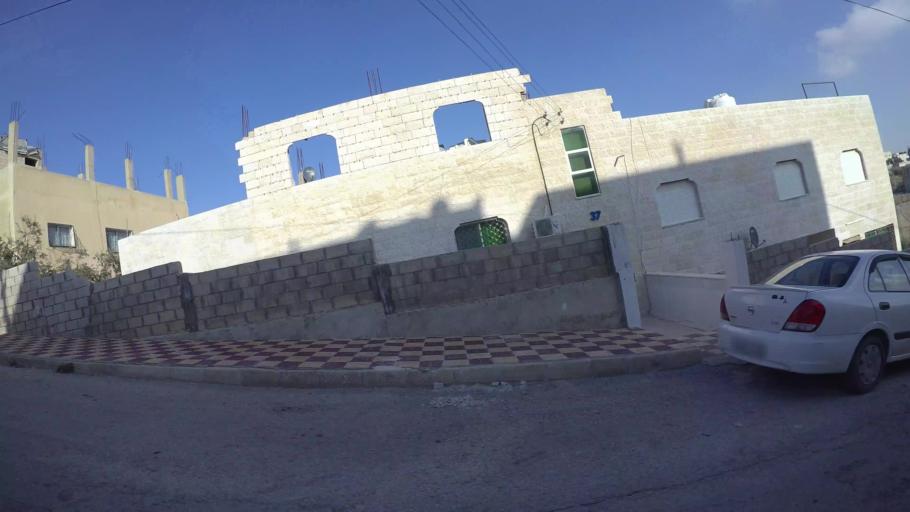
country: JO
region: Amman
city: Al Bunayyat ash Shamaliyah
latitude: 31.8971
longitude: 35.9205
